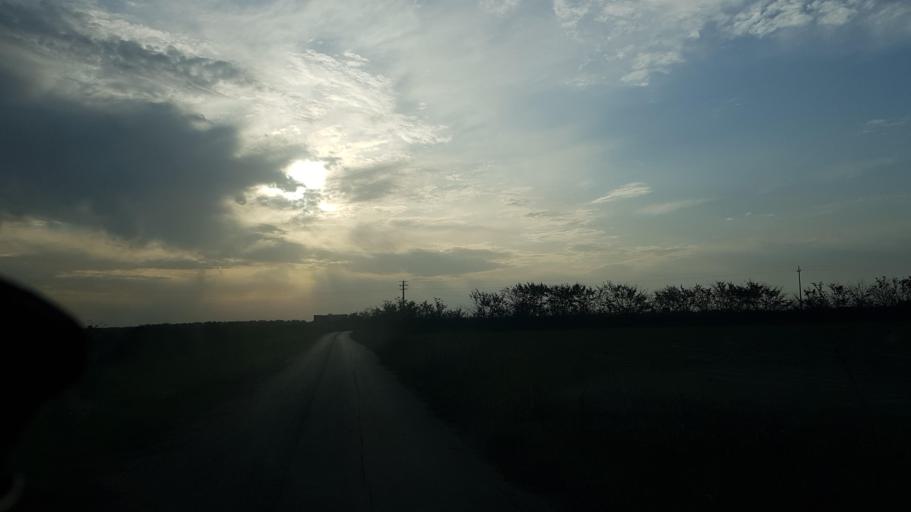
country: IT
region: Apulia
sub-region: Provincia di Brindisi
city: Mesagne
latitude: 40.5266
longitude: 17.8357
